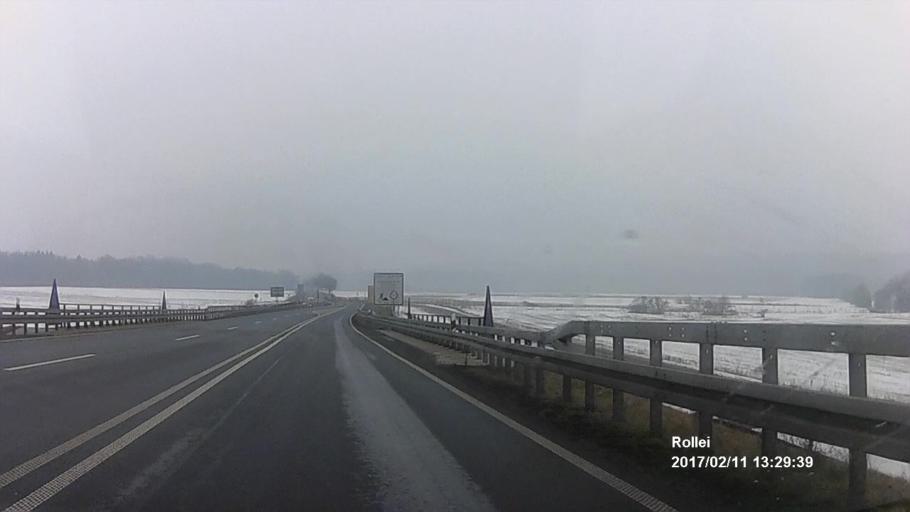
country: DE
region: Lower Saxony
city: Bad Sachsa
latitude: 51.5782
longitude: 10.5149
